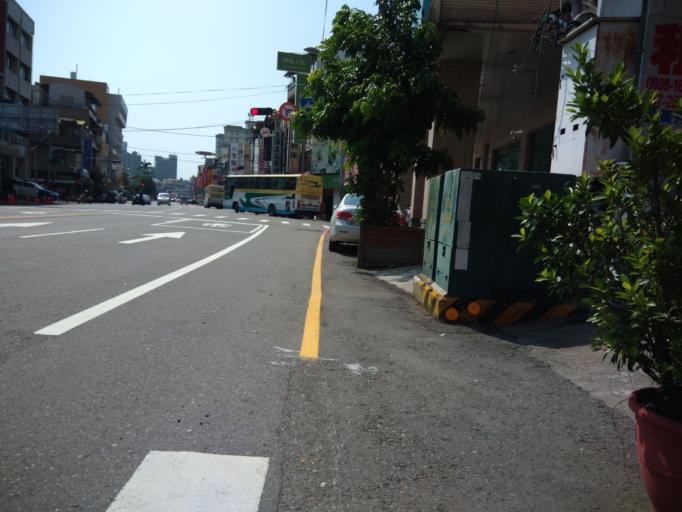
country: TW
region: Taiwan
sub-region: Changhua
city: Chang-hua
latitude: 24.0780
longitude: 120.5444
